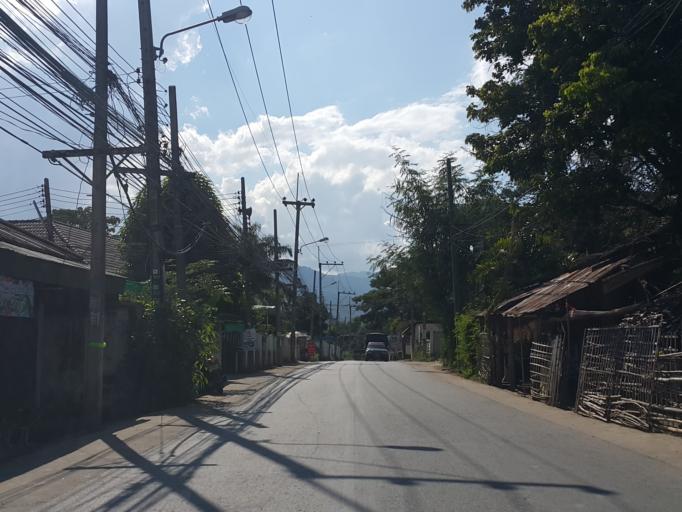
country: TH
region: Chiang Mai
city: San Sai
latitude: 18.9132
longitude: 98.9380
